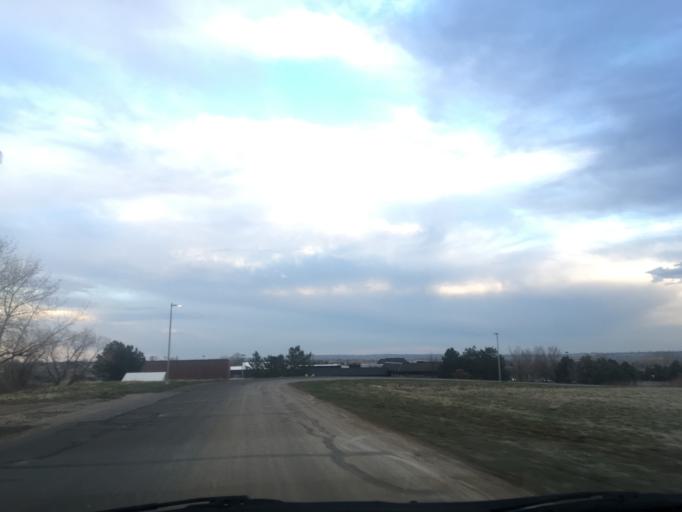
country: US
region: Colorado
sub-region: Boulder County
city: Lafayette
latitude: 39.9590
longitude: -105.0449
